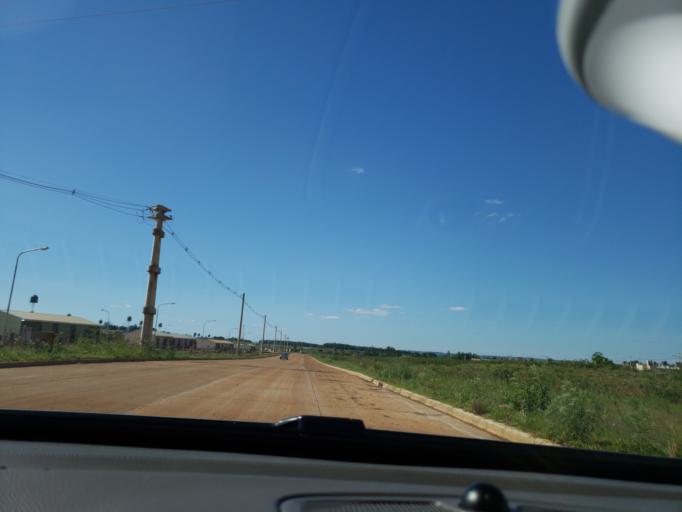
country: AR
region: Misiones
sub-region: Departamento de Capital
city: Posadas
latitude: -27.4031
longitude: -55.9886
